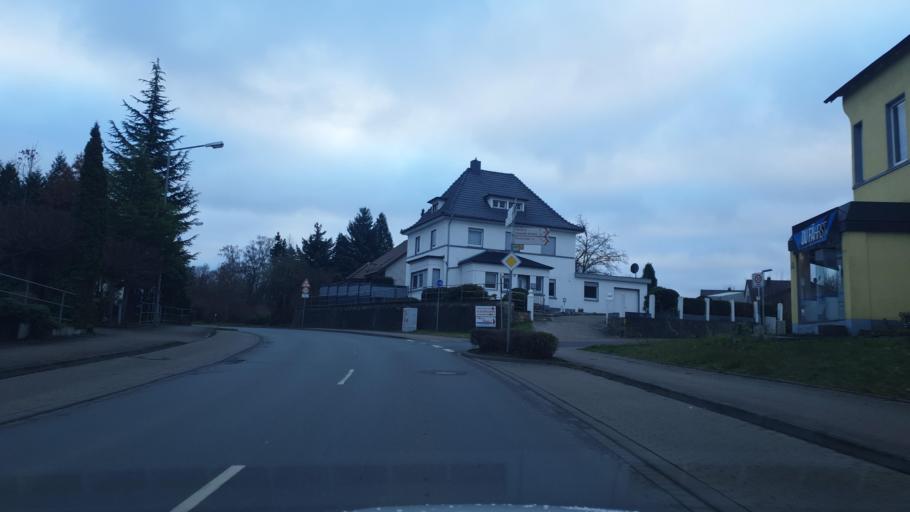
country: DE
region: North Rhine-Westphalia
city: Loehne
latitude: 52.1882
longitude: 8.6886
